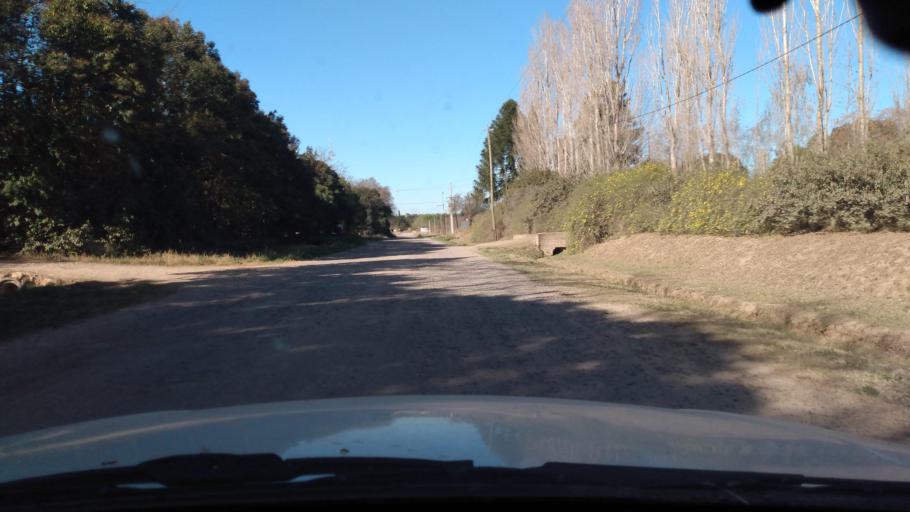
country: AR
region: Buenos Aires
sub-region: Partido de Mercedes
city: Mercedes
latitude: -34.6484
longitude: -59.3985
